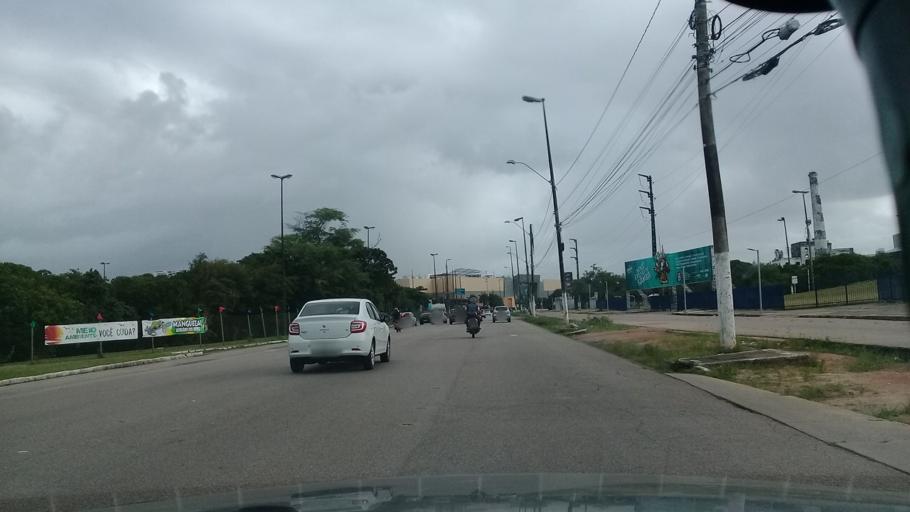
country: BR
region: Pernambuco
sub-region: Recife
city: Recife
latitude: -8.0336
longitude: -34.8690
